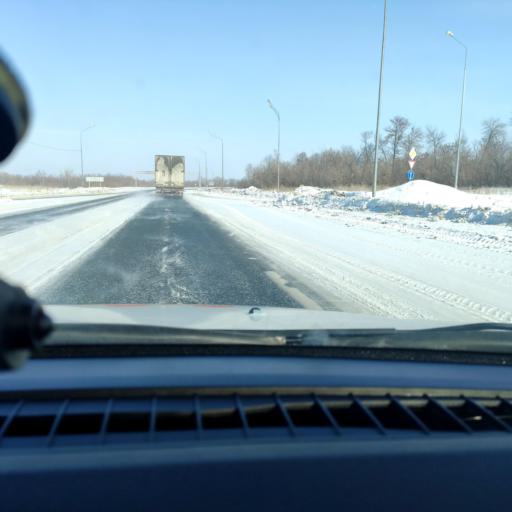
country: RU
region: Samara
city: Smyshlyayevka
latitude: 53.1508
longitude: 50.3948
